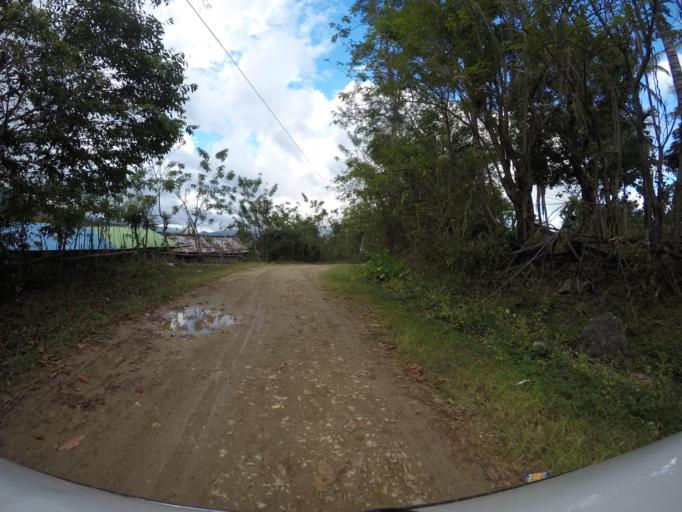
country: TL
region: Baucau
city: Venilale
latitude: -8.6825
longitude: 126.6492
